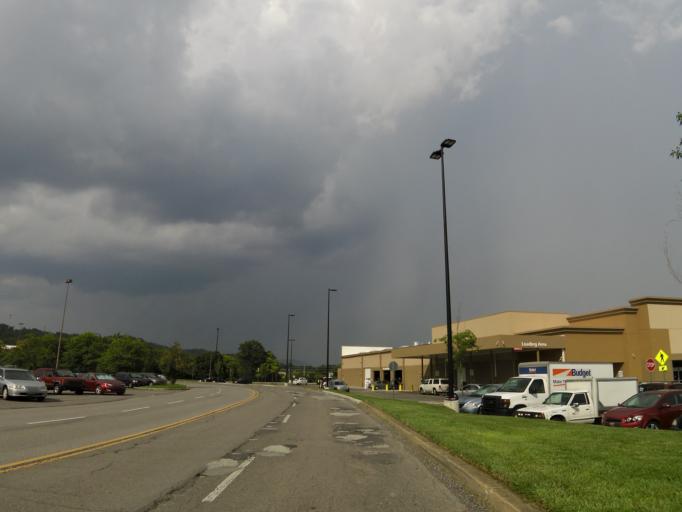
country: US
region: Tennessee
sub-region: Knox County
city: Knoxville
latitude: 36.0323
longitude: -83.8733
